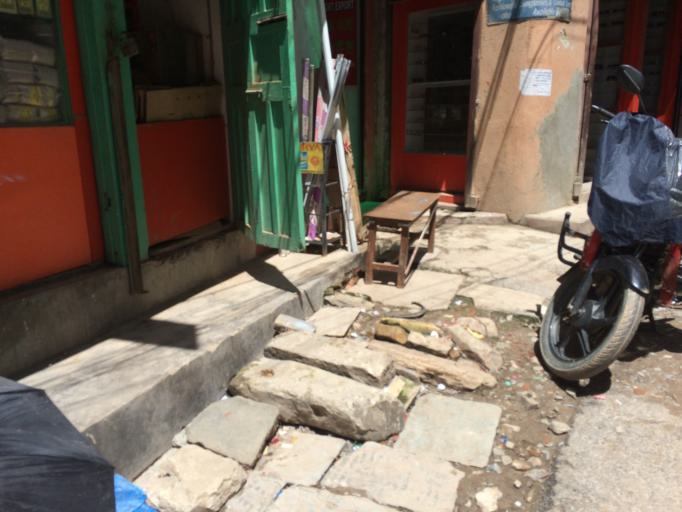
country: NP
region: Central Region
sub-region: Bagmati Zone
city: Kathmandu
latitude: 27.7103
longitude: 85.3110
